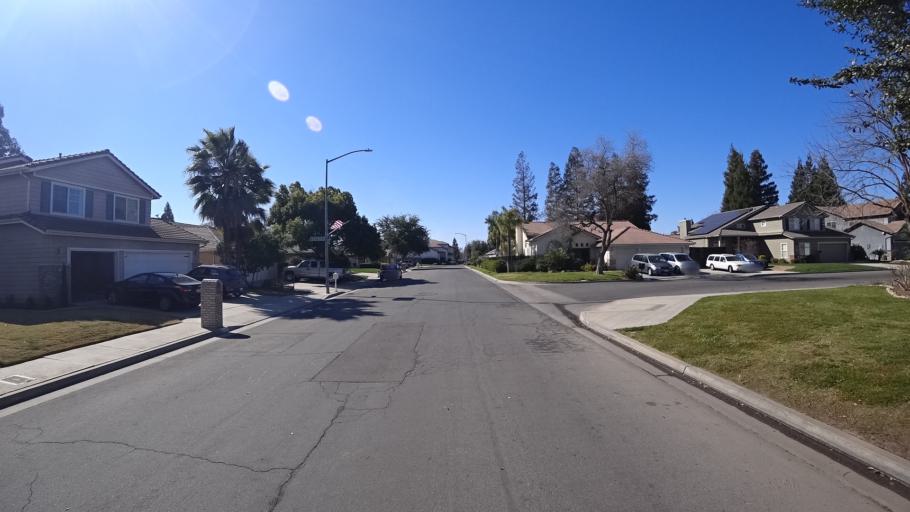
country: US
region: California
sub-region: Fresno County
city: Clovis
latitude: 36.8634
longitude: -119.7438
